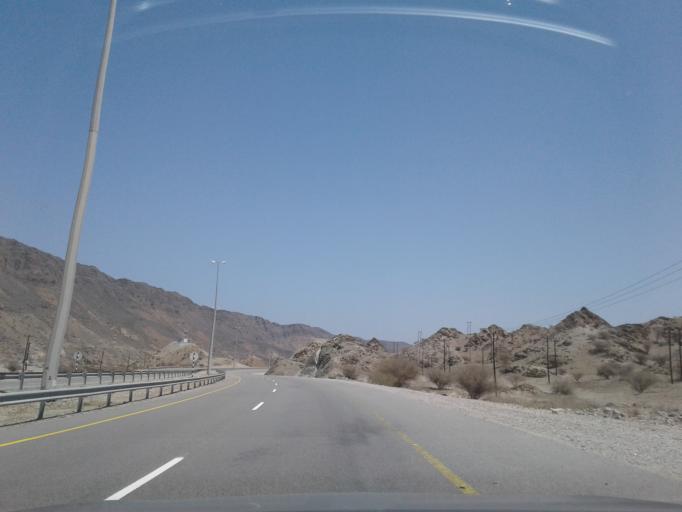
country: OM
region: Muhafazat Masqat
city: Muscat
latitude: 23.2648
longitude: 58.7592
